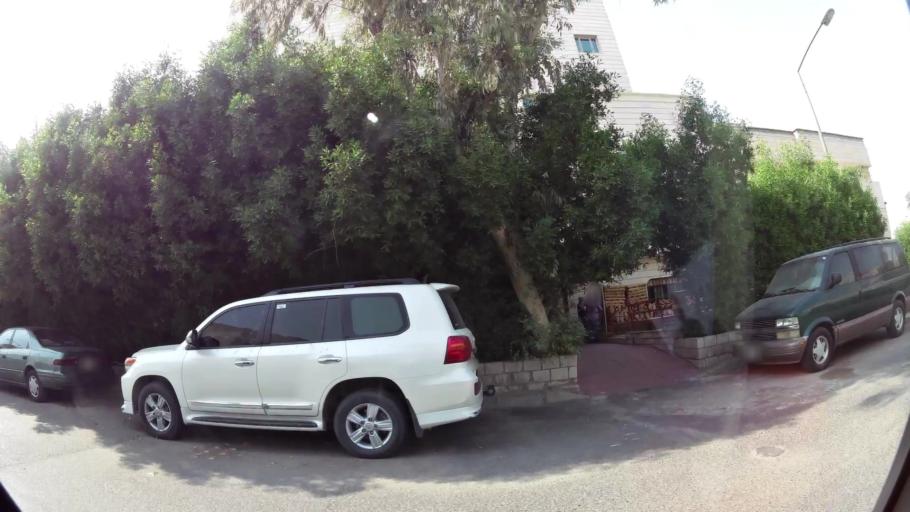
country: KW
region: Muhafazat al Jahra'
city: Al Jahra'
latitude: 29.3329
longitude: 47.6517
